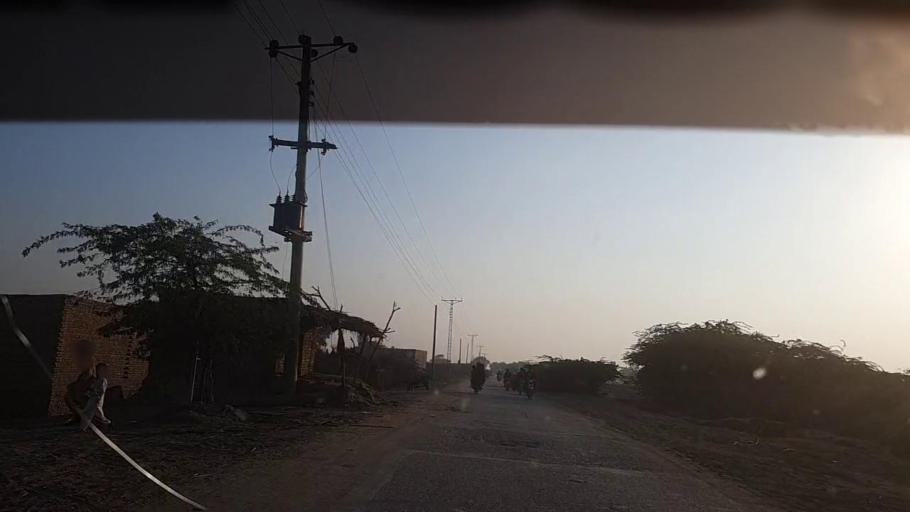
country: PK
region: Sindh
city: Ranipur
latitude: 27.2769
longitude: 68.5144
